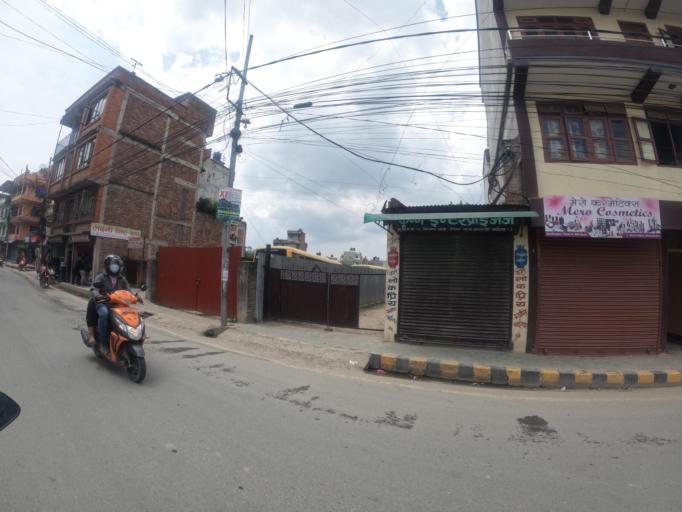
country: NP
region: Central Region
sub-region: Bagmati Zone
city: Bhaktapur
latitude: 27.6876
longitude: 85.3886
